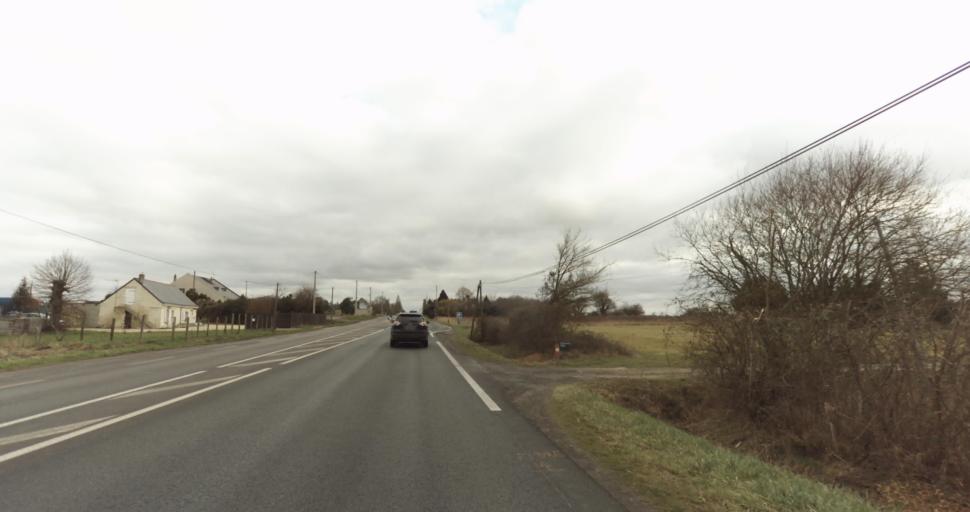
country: FR
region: Pays de la Loire
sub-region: Departement de Maine-et-Loire
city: Vivy
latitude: 47.3628
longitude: -0.0914
